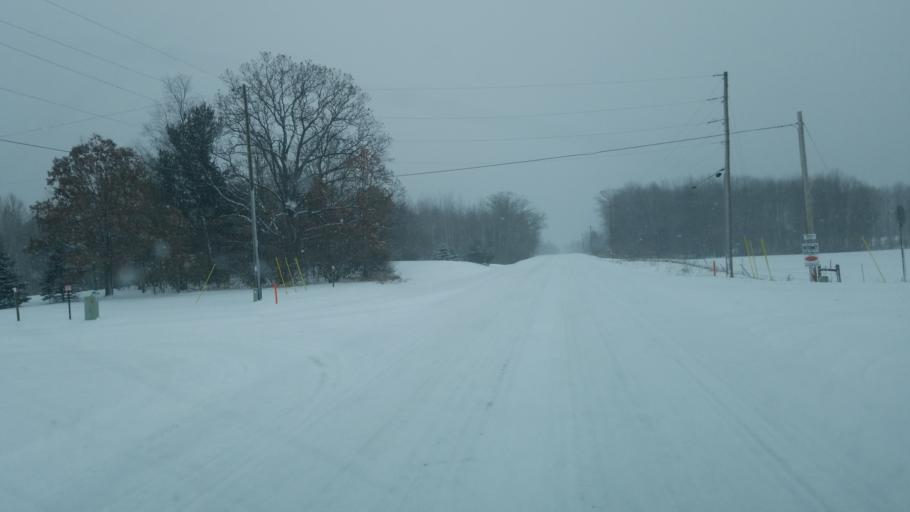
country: US
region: Michigan
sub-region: Mecosta County
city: Canadian Lakes
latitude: 43.5761
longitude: -85.3446
